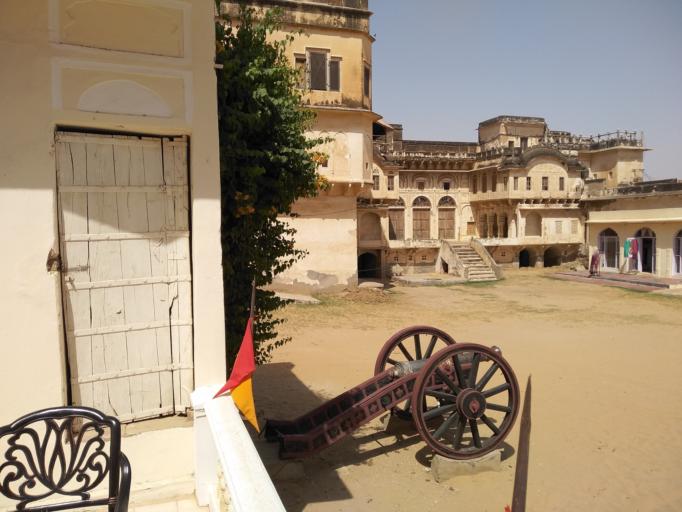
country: IN
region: Rajasthan
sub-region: Sikar
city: Fatehpur
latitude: 28.0538
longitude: 75.1485
